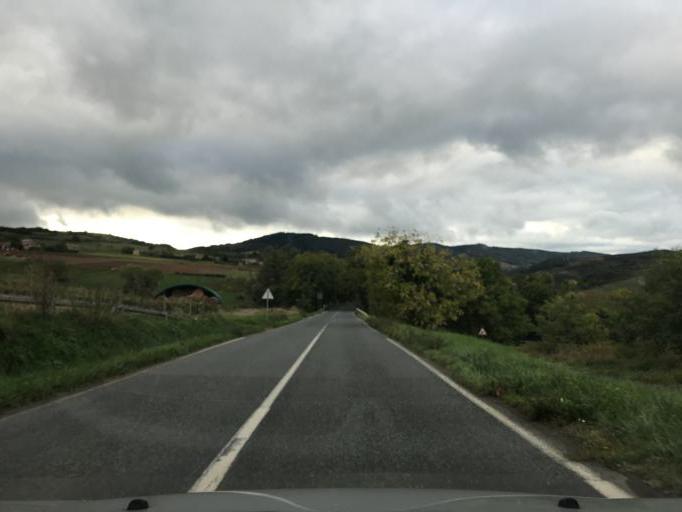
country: FR
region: Rhone-Alpes
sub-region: Departement du Rhone
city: Cogny
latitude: 45.9993
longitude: 4.6252
